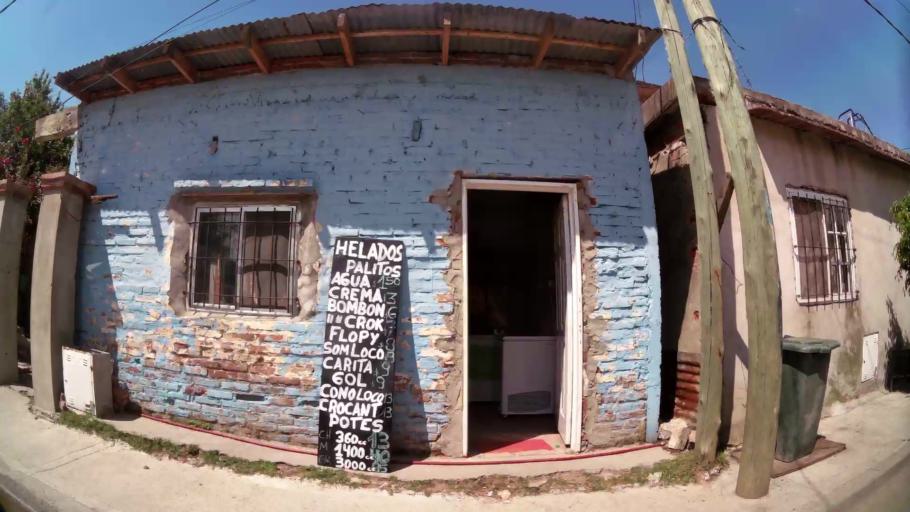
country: AR
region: Buenos Aires
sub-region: Partido de Tigre
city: Tigre
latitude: -34.4662
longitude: -58.5987
